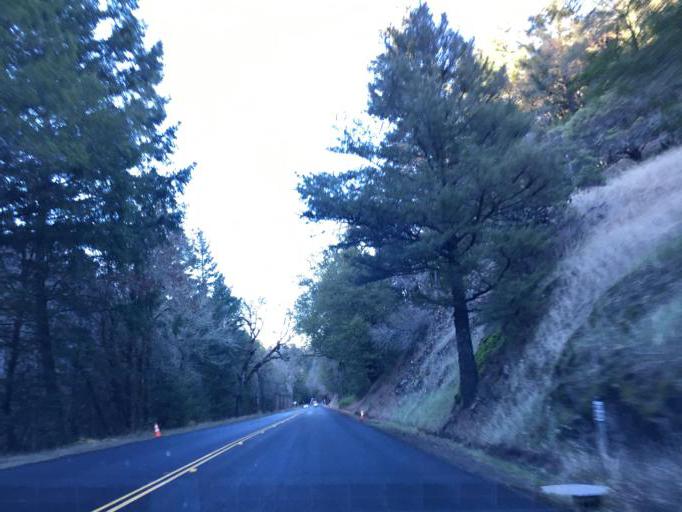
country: US
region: California
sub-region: Mendocino County
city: Laytonville
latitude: 39.8104
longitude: -123.5553
